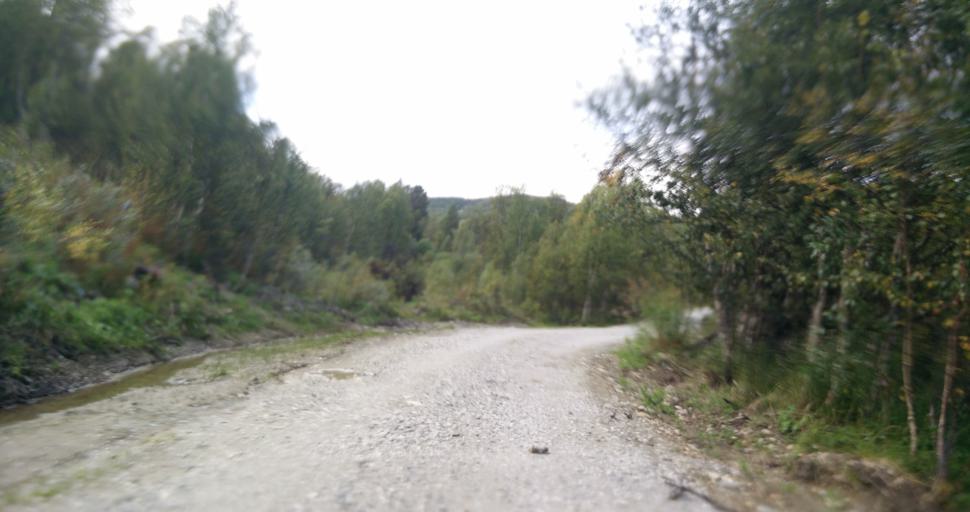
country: NO
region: Sor-Trondelag
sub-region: Tydal
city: Aas
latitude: 62.6382
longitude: 12.4178
